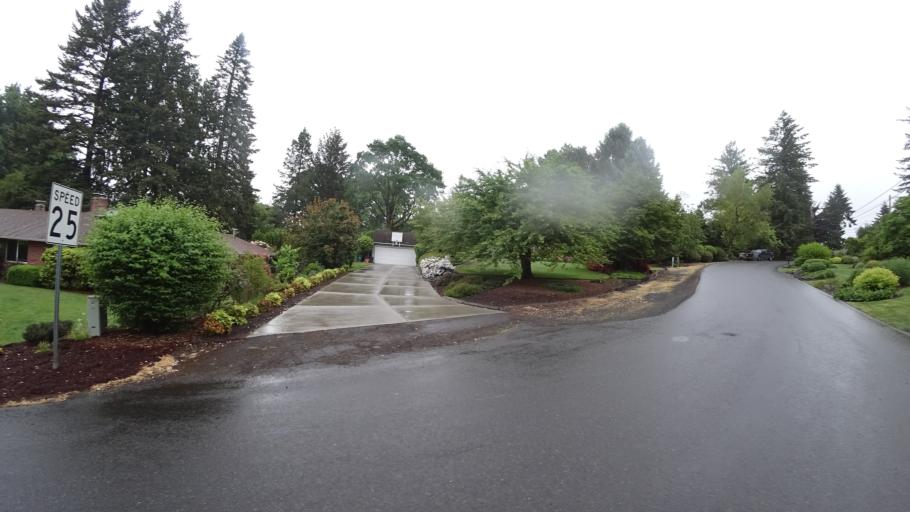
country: US
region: Oregon
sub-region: Washington County
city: Raleigh Hills
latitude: 45.4763
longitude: -122.7710
